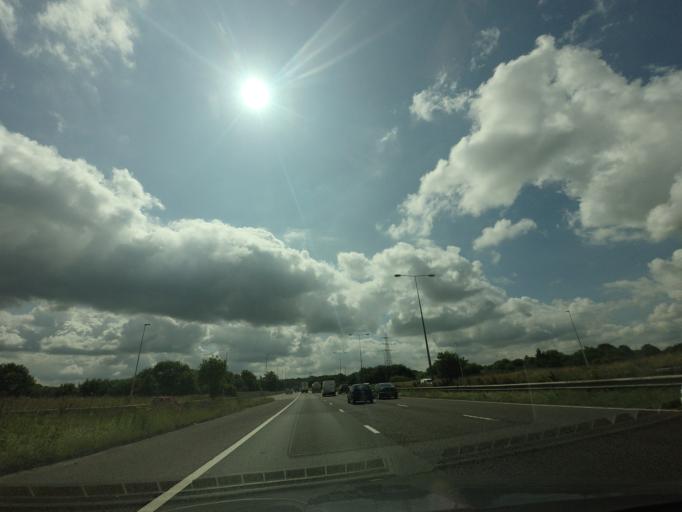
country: GB
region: England
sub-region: St. Helens
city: Billinge
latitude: 53.5316
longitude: -2.6983
